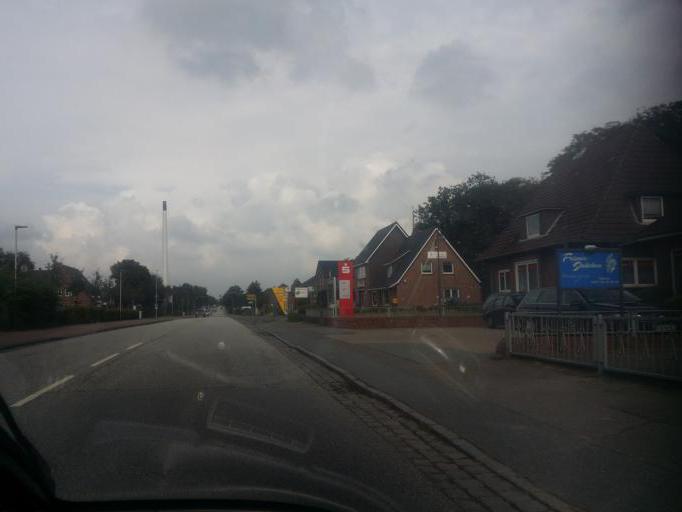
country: DE
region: Schleswig-Holstein
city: Hemmingstedt
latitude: 54.1465
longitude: 9.0714
